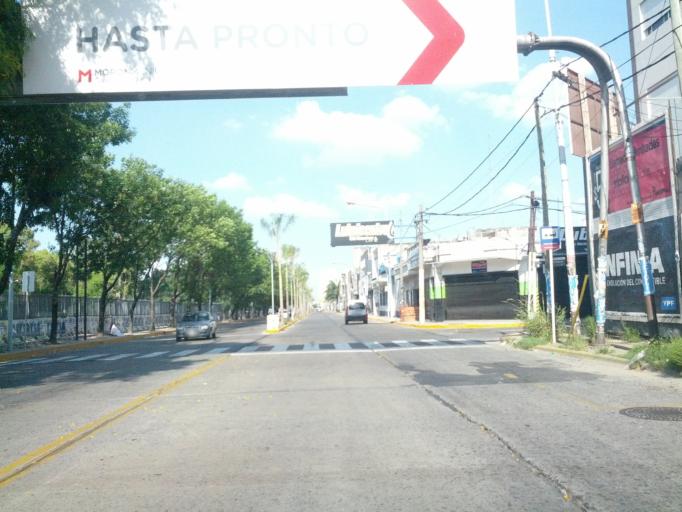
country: AR
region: Buenos Aires
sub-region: Partido de Moron
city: Moron
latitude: -34.6436
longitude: -58.5822
